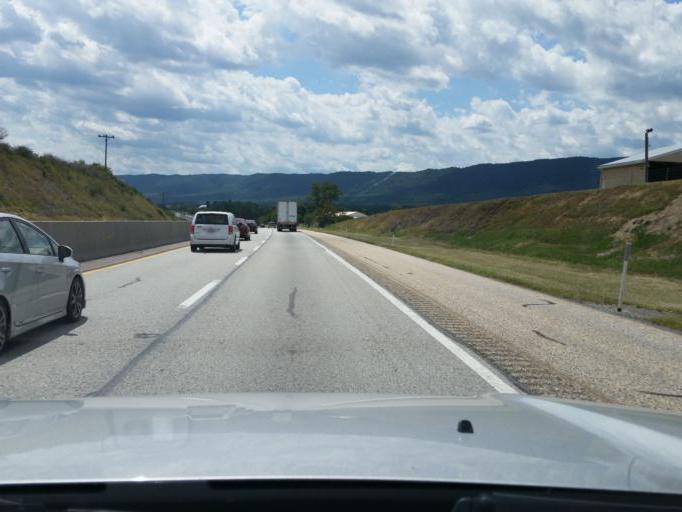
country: US
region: Pennsylvania
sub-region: Franklin County
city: Doylestown
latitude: 40.1223
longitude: -77.7692
